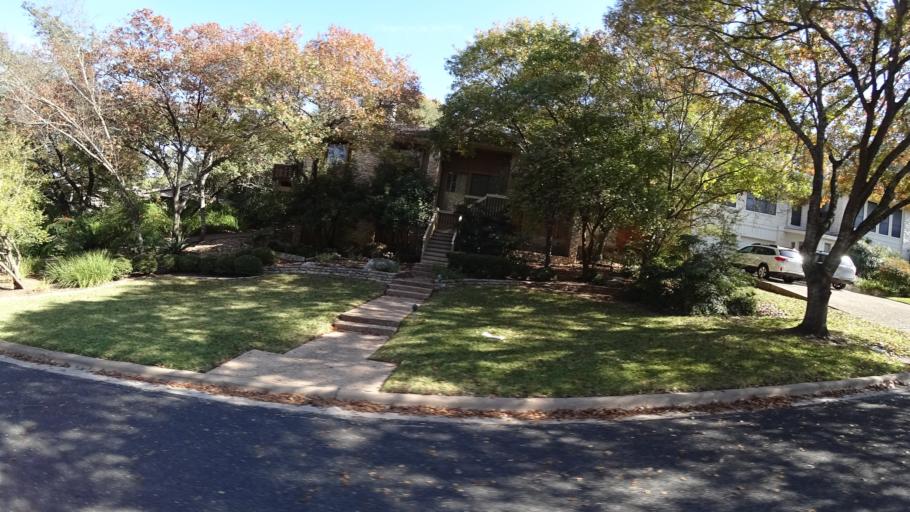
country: US
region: Texas
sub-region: Williamson County
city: Jollyville
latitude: 30.3693
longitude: -97.7699
